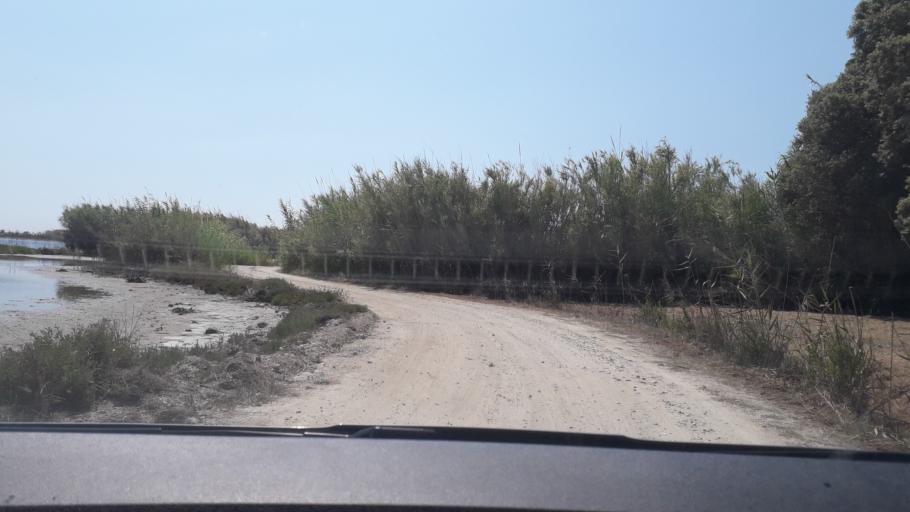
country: GR
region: Ionian Islands
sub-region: Nomos Kerkyras
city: Agios Matthaios
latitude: 39.4554
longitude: 19.8796
